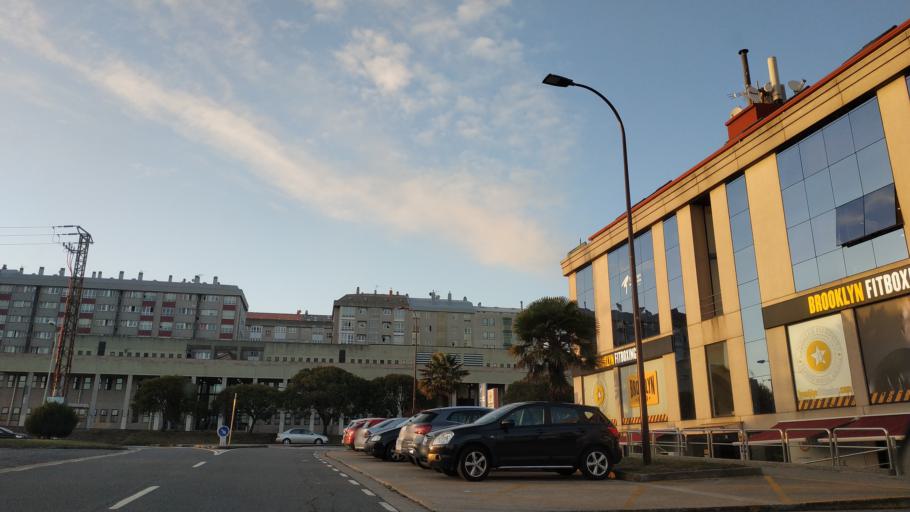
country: ES
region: Galicia
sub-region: Provincia da Coruna
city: A Coruna
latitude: 43.3573
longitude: -8.4224
